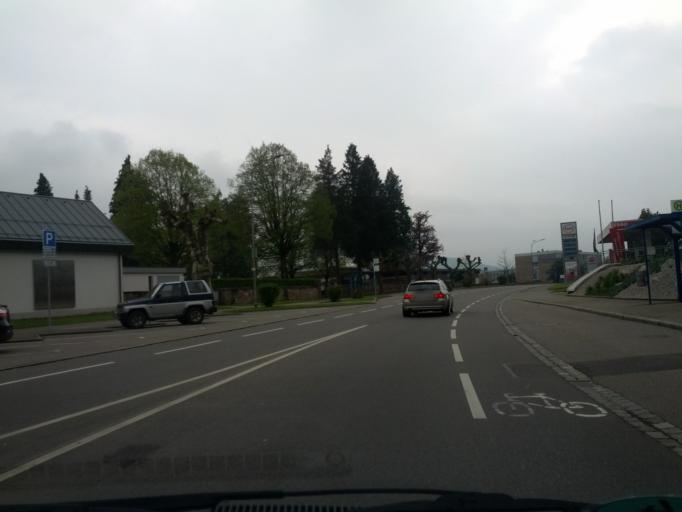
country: DE
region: Baden-Wuerttemberg
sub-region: Freiburg Region
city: Schopfheim
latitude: 47.6481
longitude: 7.8153
